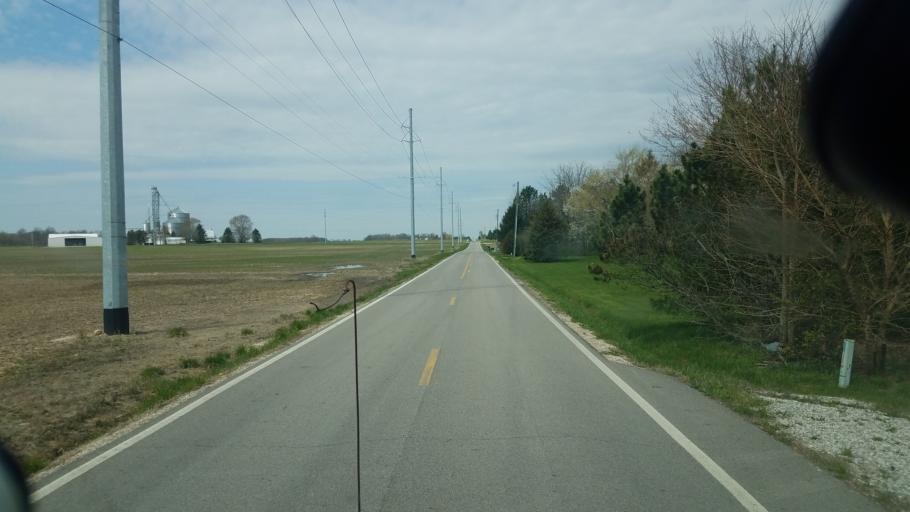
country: US
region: Ohio
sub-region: Delaware County
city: Delaware
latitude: 40.3656
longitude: -83.0966
